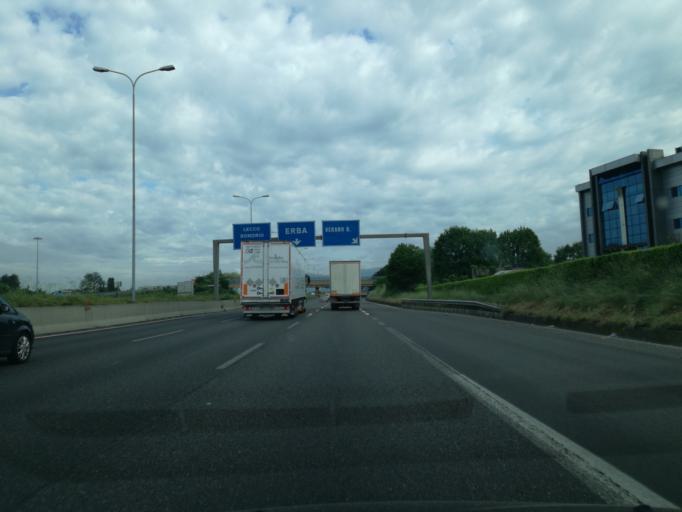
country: IT
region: Lombardy
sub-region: Provincia di Monza e Brianza
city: Verano Brianza
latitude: 45.6754
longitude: 9.2194
